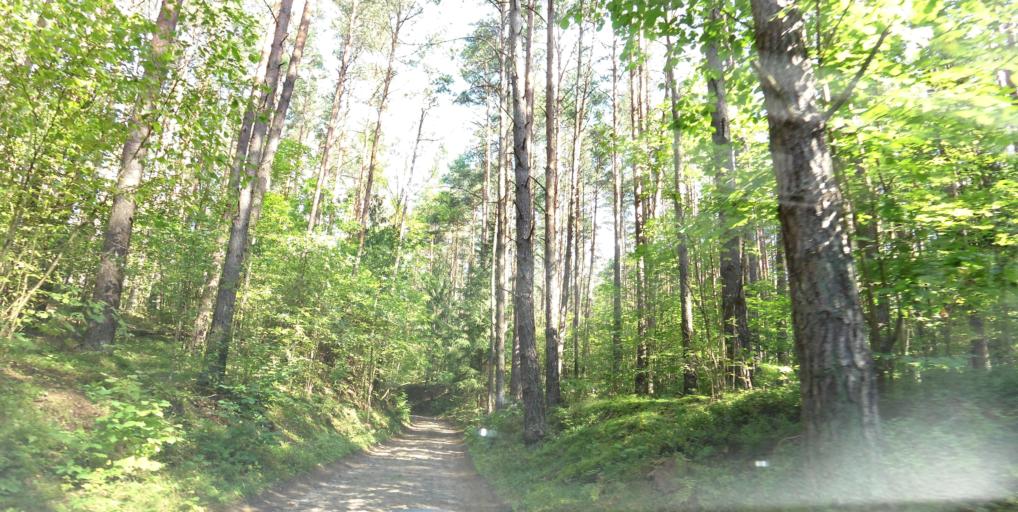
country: LT
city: Grigiskes
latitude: 54.7364
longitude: 25.0400
